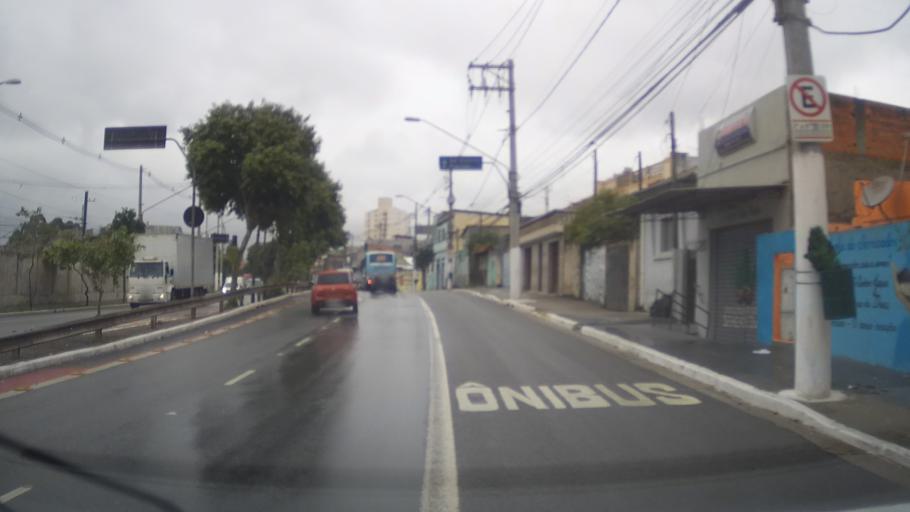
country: BR
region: Sao Paulo
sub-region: Guarulhos
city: Guarulhos
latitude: -23.4848
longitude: -46.4887
